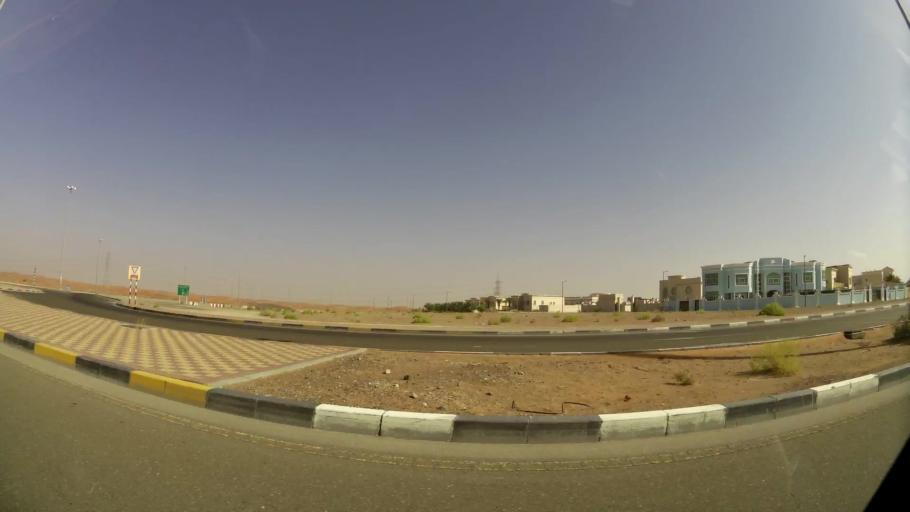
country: OM
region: Al Buraimi
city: Al Buraymi
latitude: 24.3442
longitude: 55.7808
